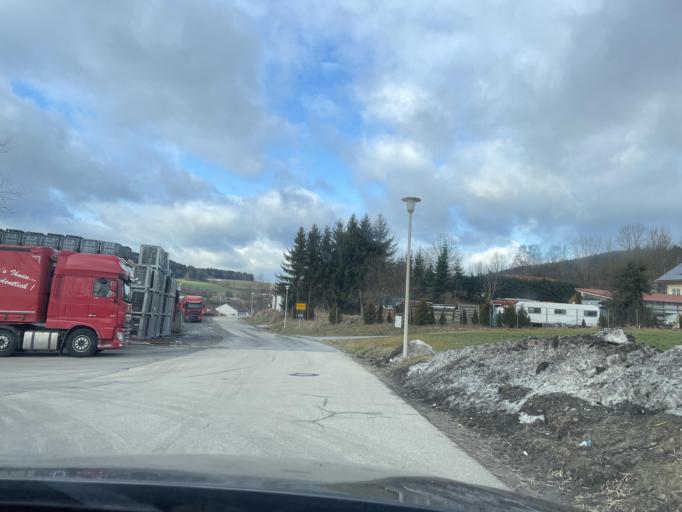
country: DE
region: Bavaria
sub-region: Lower Bavaria
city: Prackenbach
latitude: 49.0929
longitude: 12.8322
